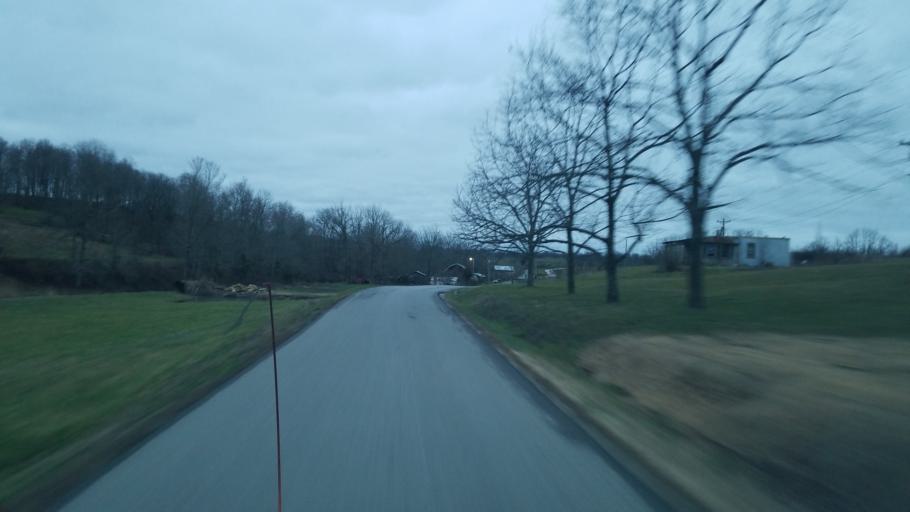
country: US
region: Kentucky
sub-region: Fleming County
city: Flemingsburg
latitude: 38.5045
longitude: -83.6917
